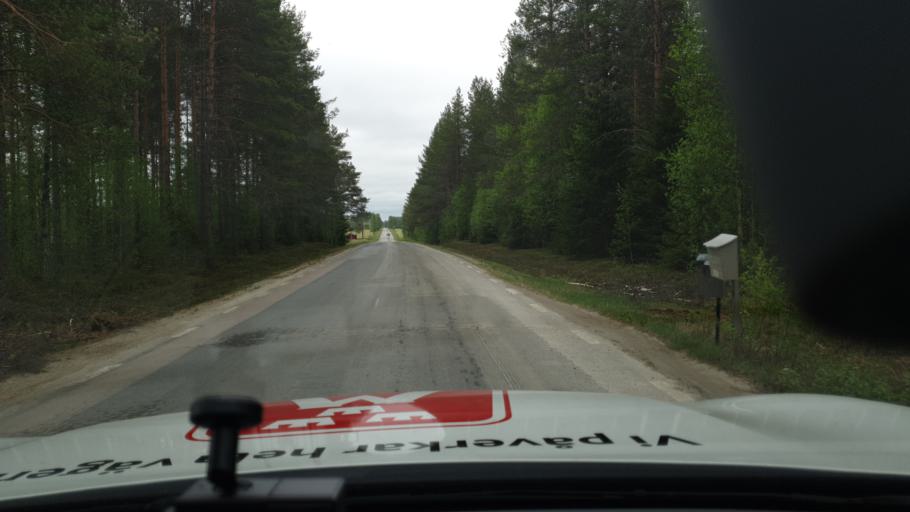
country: SE
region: Vaesterbotten
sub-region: Vannas Kommun
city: Vannasby
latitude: 63.9807
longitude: 19.8764
